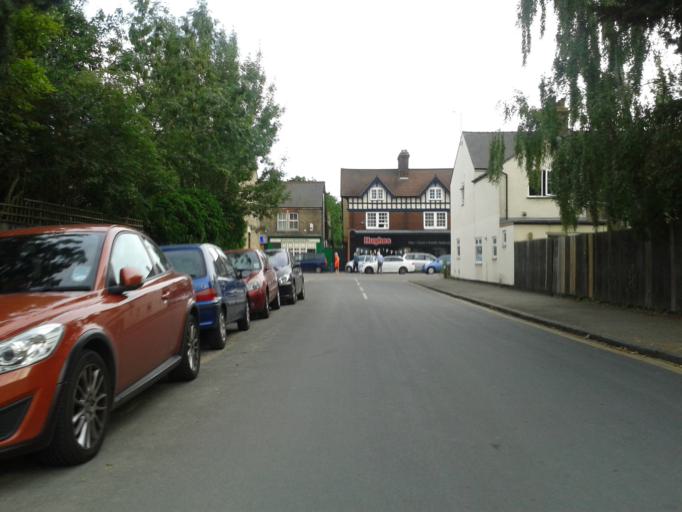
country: GB
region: England
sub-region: Cambridgeshire
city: Cambridge
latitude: 52.1893
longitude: 0.1397
